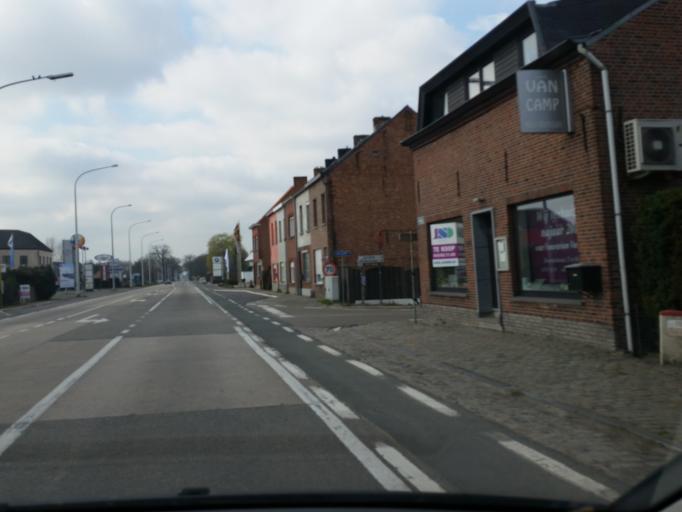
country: BE
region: Flanders
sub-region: Provincie Vlaams-Brabant
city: Boortmeerbeek
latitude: 50.9835
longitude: 4.5494
